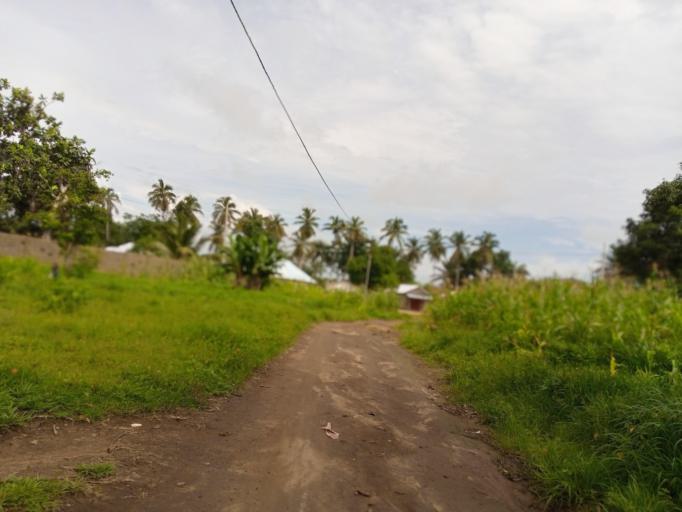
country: SL
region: Northern Province
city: Masoyila
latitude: 8.5925
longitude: -13.1972
